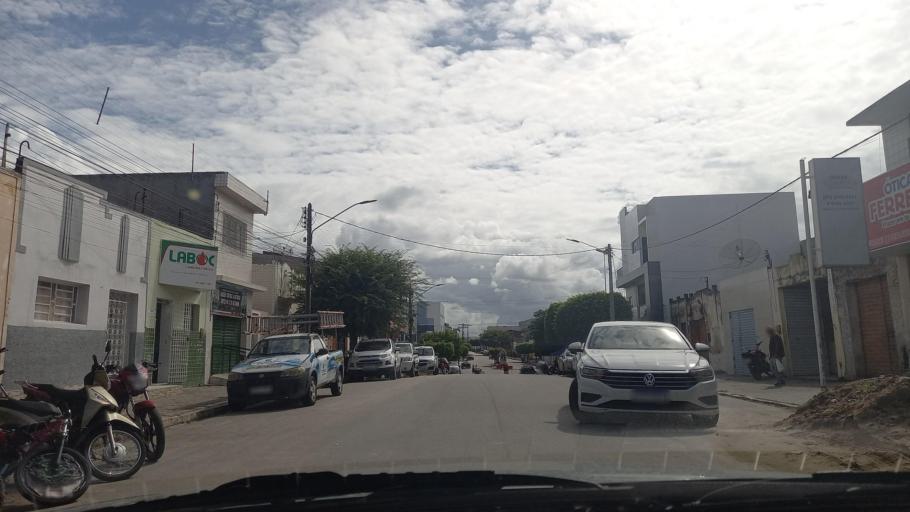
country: BR
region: Pernambuco
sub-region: Cachoeirinha
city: Cachoeirinha
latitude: -8.4884
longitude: -36.2363
